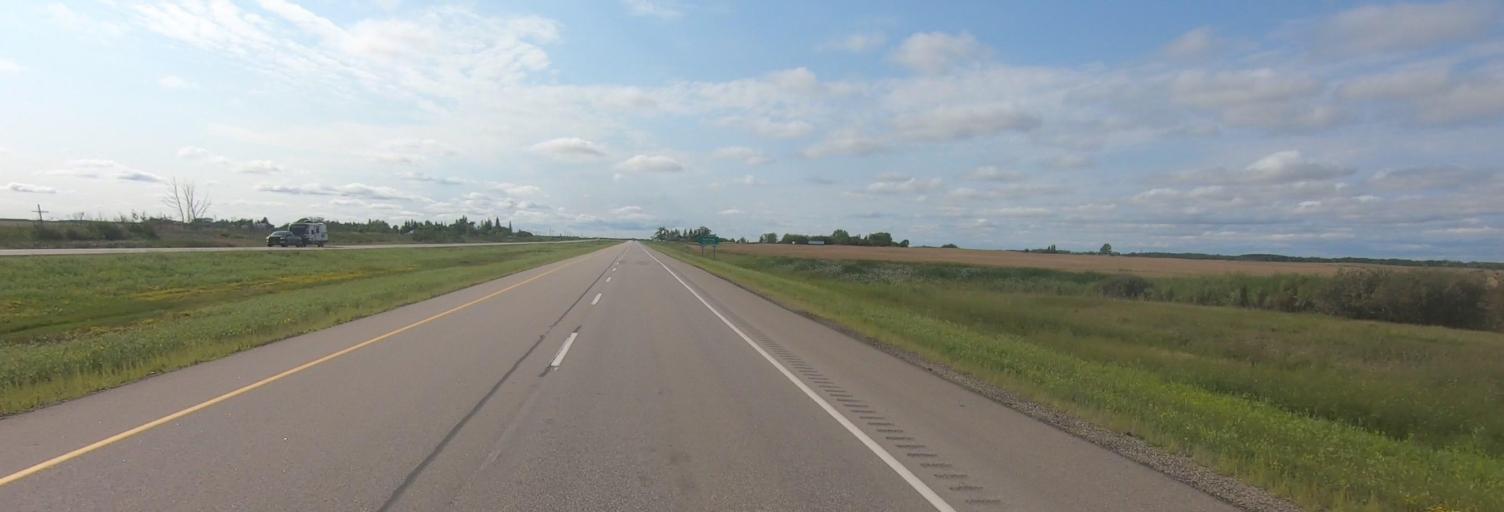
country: CA
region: Saskatchewan
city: Moosomin
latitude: 50.0714
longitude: -101.4940
